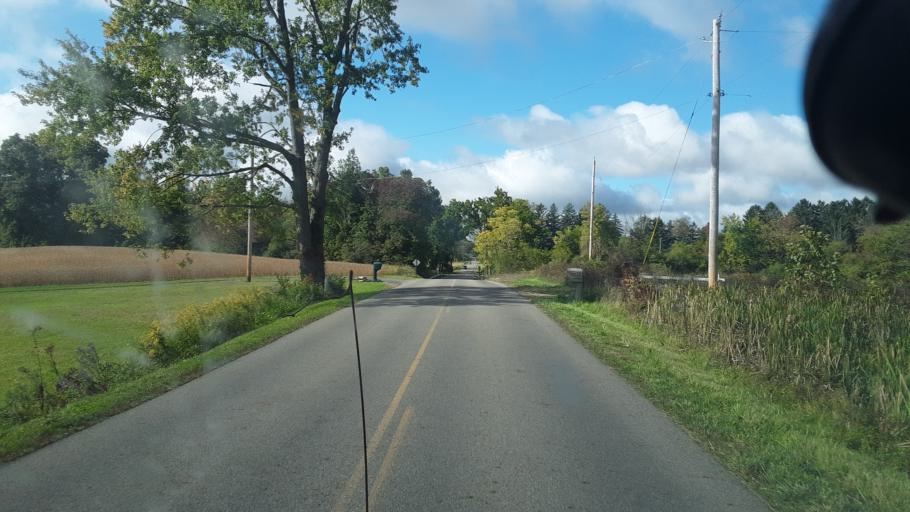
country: US
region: Ohio
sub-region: Knox County
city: Centerburg
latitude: 40.2778
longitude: -82.6493
